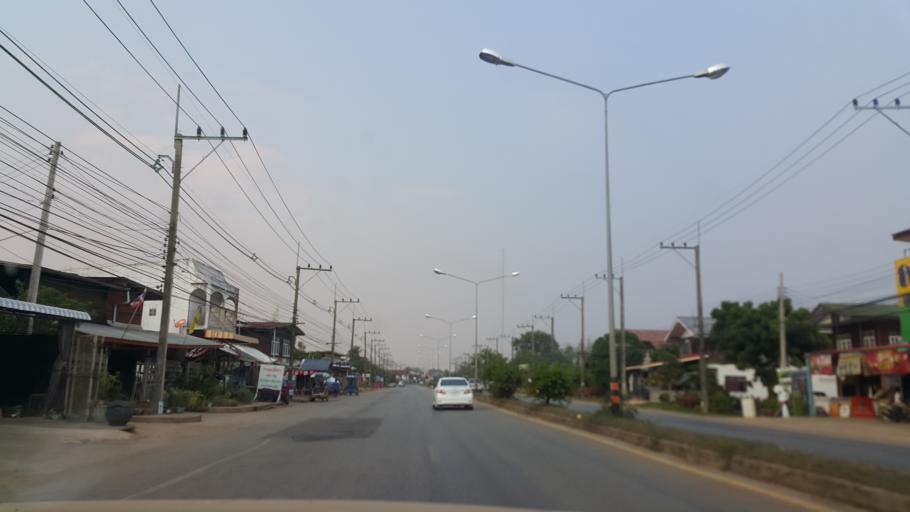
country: TH
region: Nakhon Phanom
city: That Phanom
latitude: 16.9688
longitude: 104.7274
